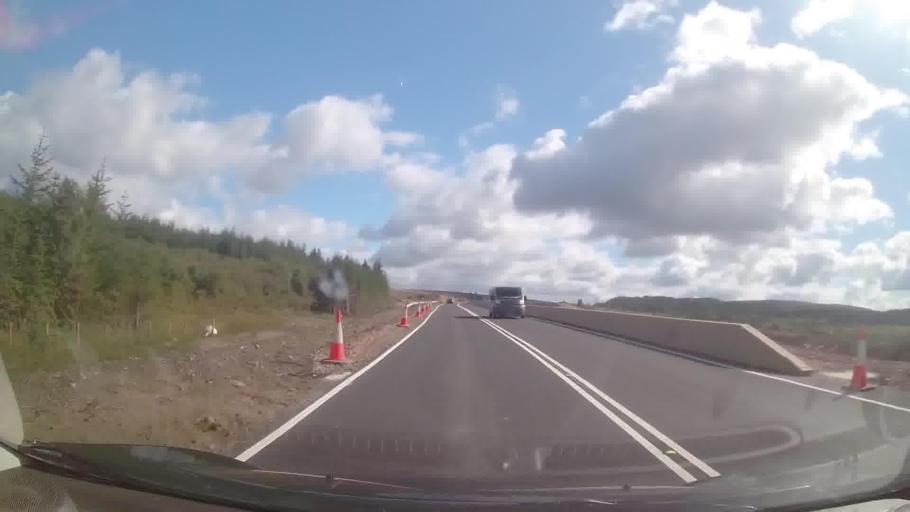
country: GB
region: Wales
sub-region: Rhondda Cynon Taf
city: Aberdare
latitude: 51.7536
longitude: -3.4562
